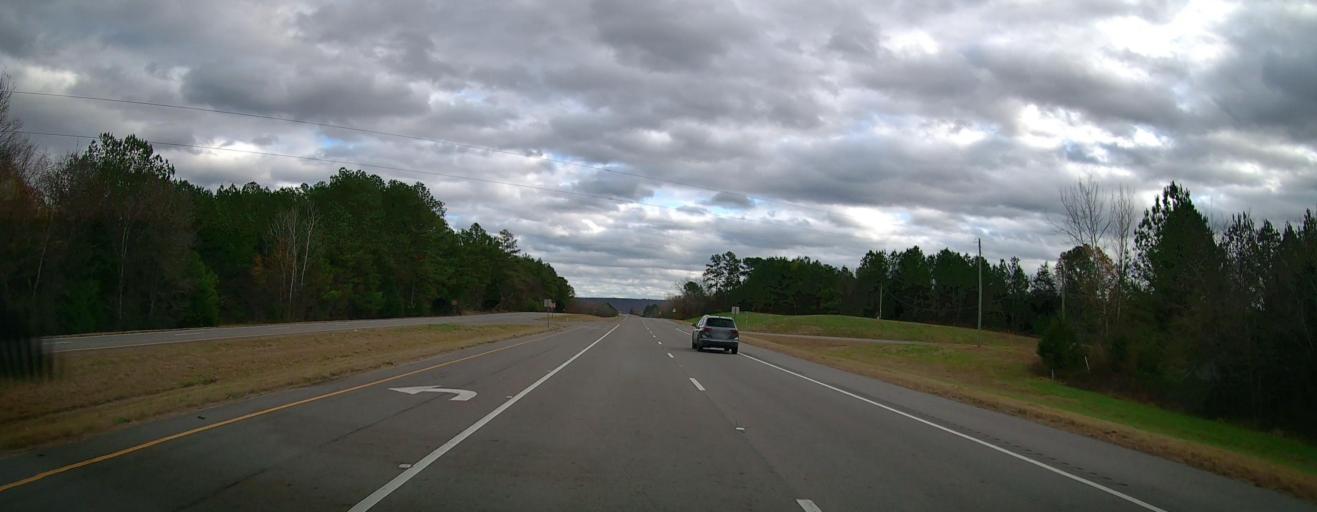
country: US
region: Alabama
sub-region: Morgan County
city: Danville
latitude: 34.3538
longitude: -87.0496
